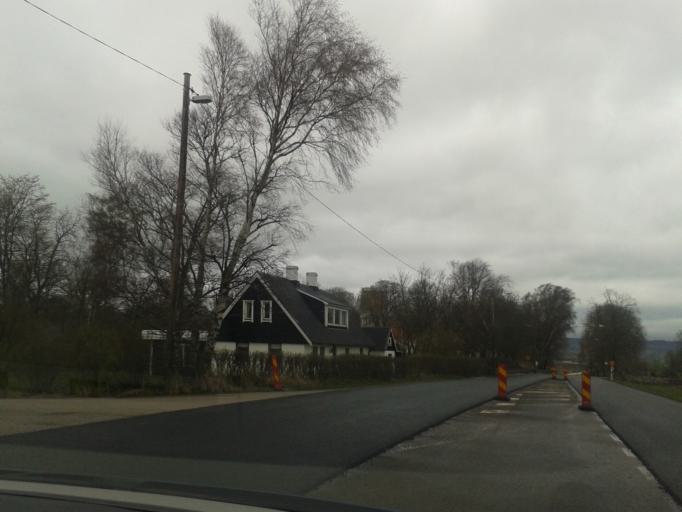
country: SE
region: Skane
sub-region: Angelholms Kommun
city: AEngelholm
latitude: 56.2937
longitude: 12.8350
